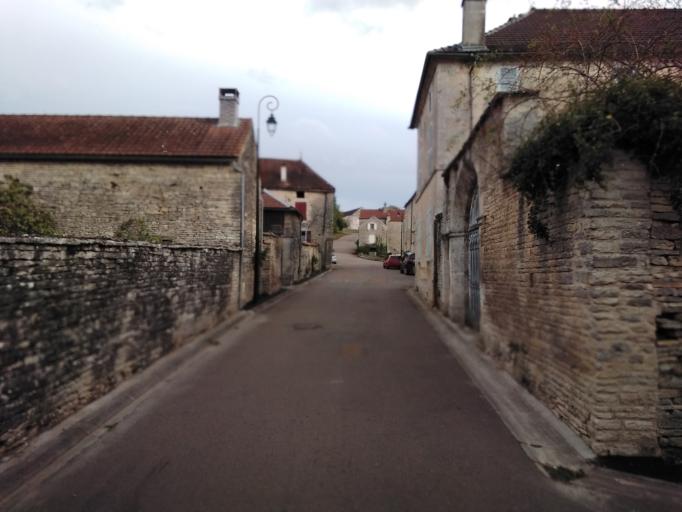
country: FR
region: Champagne-Ardenne
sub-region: Departement de l'Aube
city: Les Riceys
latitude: 47.9362
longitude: 4.3539
